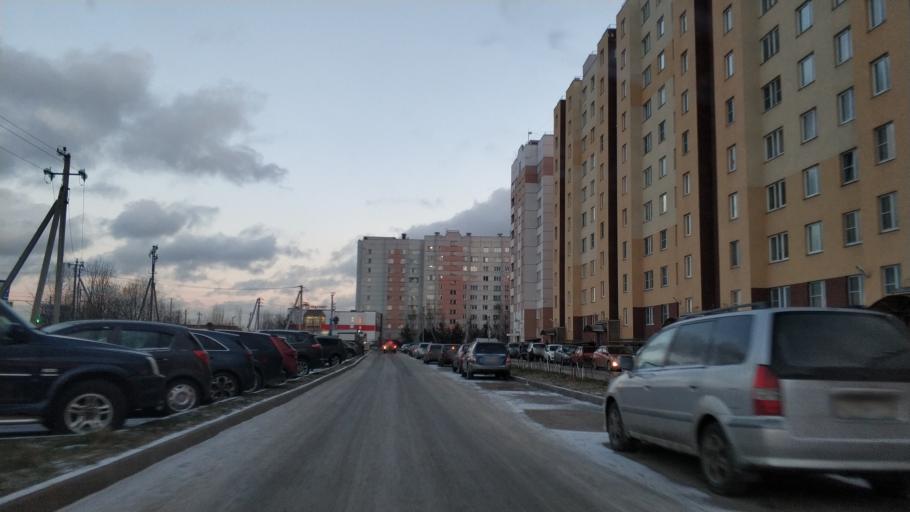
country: RU
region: St.-Petersburg
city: Pontonnyy
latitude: 59.8007
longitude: 30.6354
